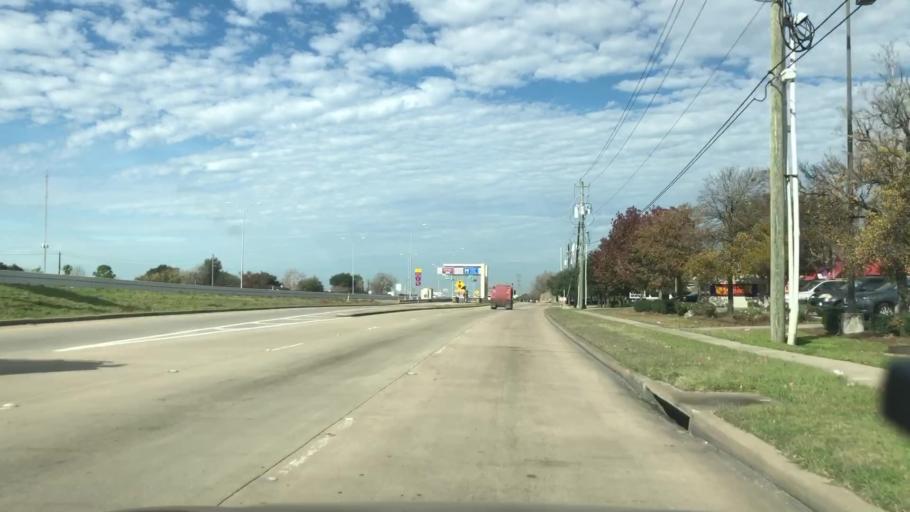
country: US
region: Texas
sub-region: Fort Bend County
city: Missouri City
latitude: 29.6151
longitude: -95.4963
